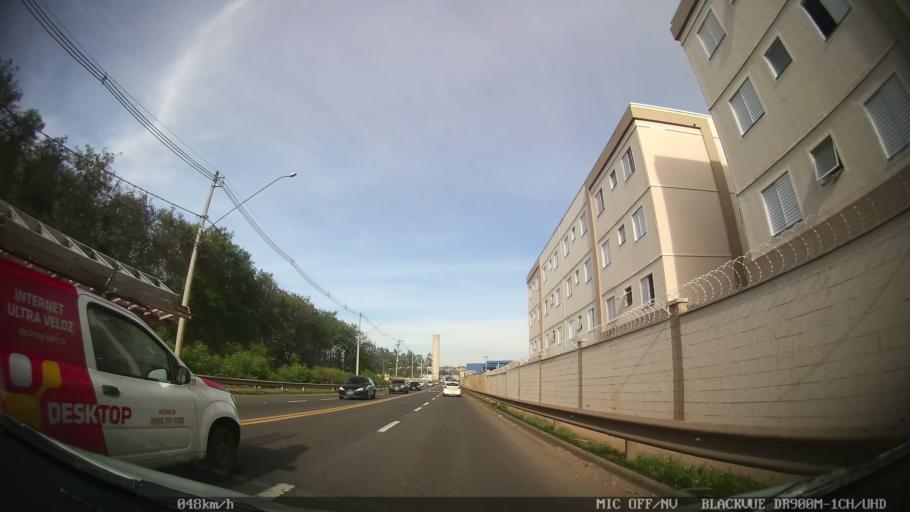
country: BR
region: Sao Paulo
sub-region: Piracicaba
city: Piracicaba
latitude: -22.6982
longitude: -47.6734
